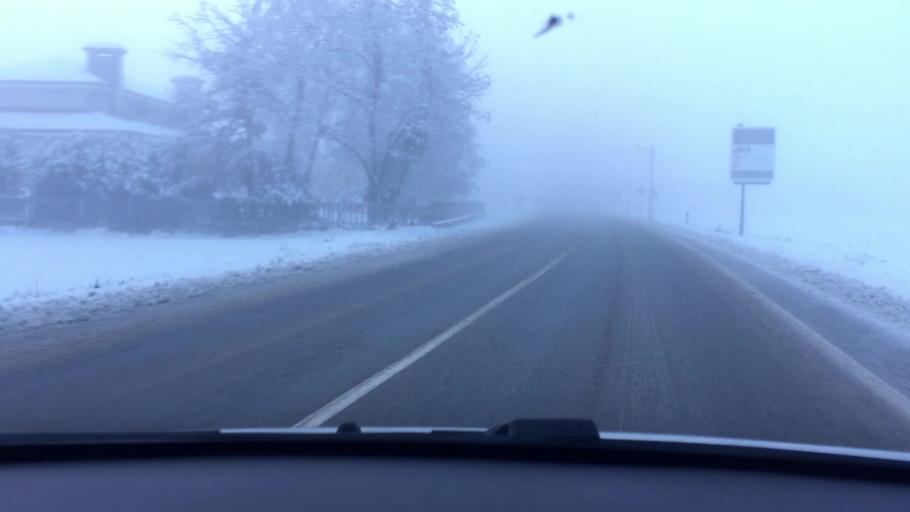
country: IT
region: Piedmont
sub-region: Provincia di Torino
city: Scalenghe
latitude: 44.8988
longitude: 7.4907
